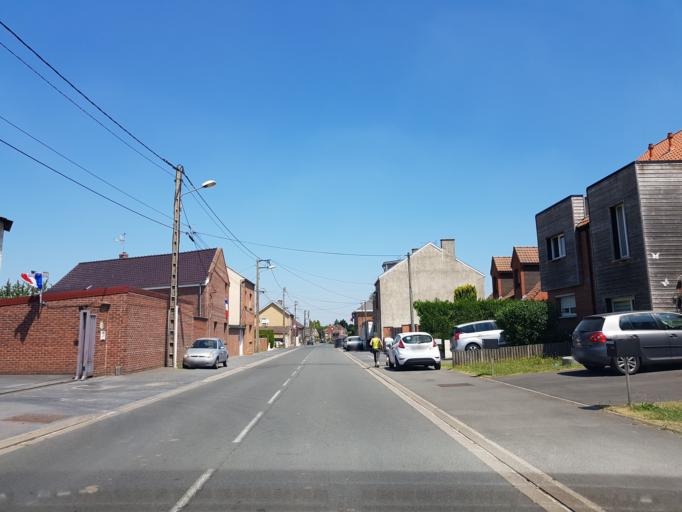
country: FR
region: Nord-Pas-de-Calais
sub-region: Departement du Nord
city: Neuville-sur-Escaut
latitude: 50.2957
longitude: 3.3565
